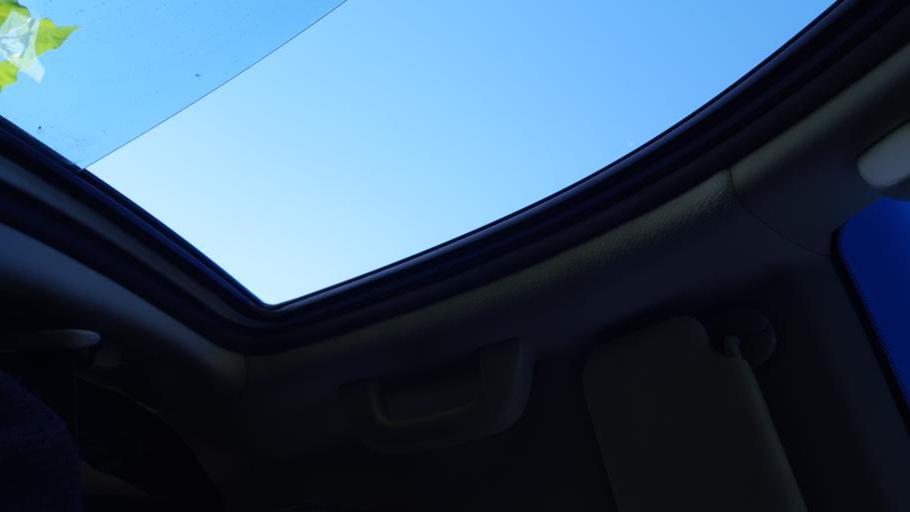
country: AR
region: Jujuy
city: La Mendieta
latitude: -24.4683
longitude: -65.0415
